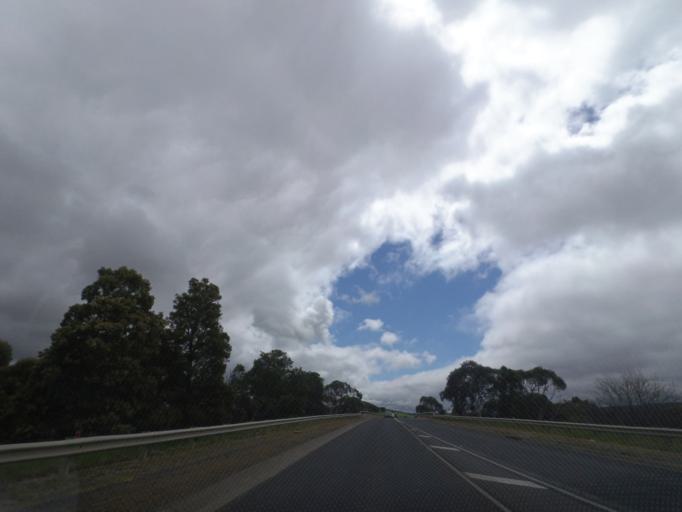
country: AU
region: Victoria
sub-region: Ballarat North
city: Lake Wendouree
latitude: -37.5216
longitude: 143.8442
